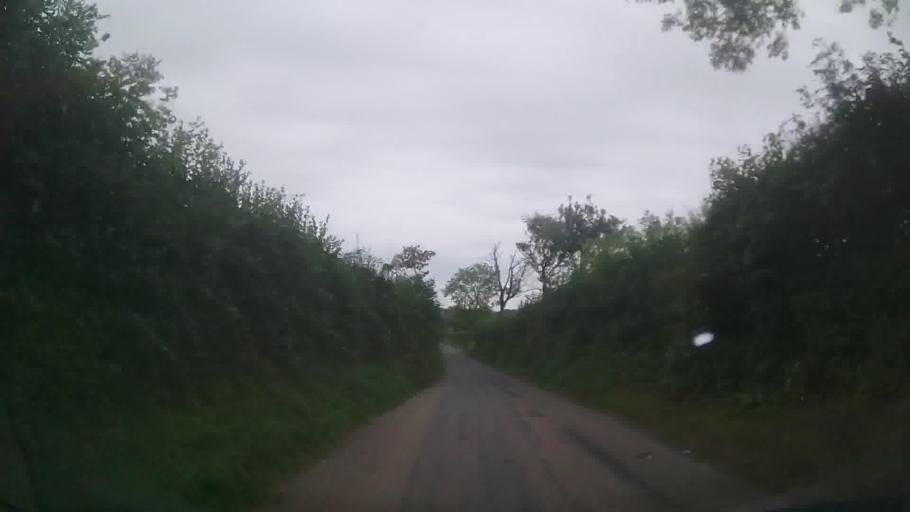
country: GB
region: Wales
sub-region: Carmarthenshire
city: Whitland
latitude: 51.7465
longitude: -4.6184
